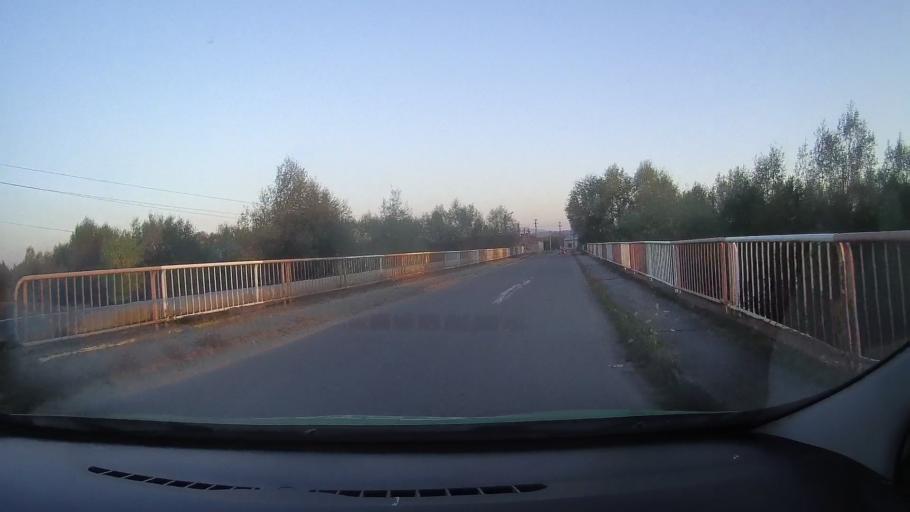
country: RO
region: Timis
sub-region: Comuna Manastiur
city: Manastiur
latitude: 45.8348
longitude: 22.0666
